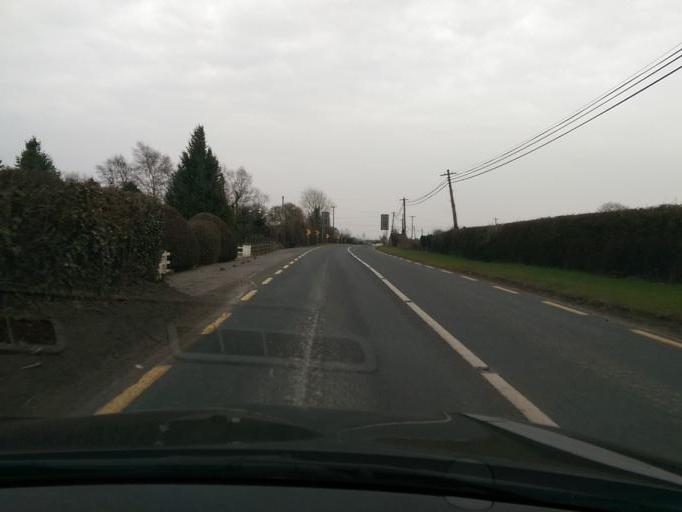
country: IE
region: Leinster
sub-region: An Iarmhi
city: Athlone
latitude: 53.4458
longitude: -7.8874
